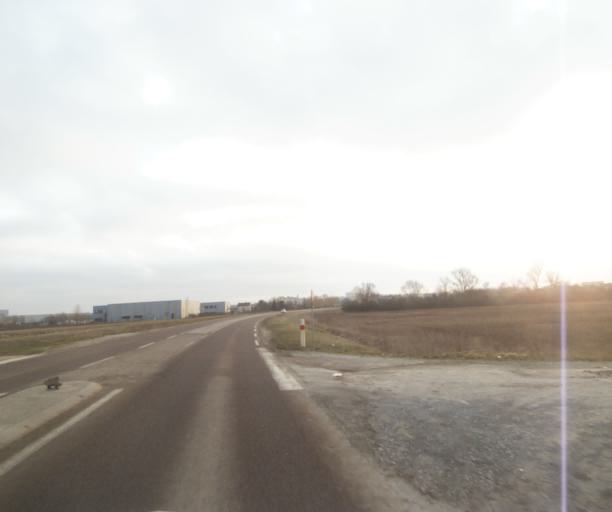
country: FR
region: Champagne-Ardenne
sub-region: Departement de la Haute-Marne
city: Saint-Dizier
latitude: 48.6498
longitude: 4.9504
